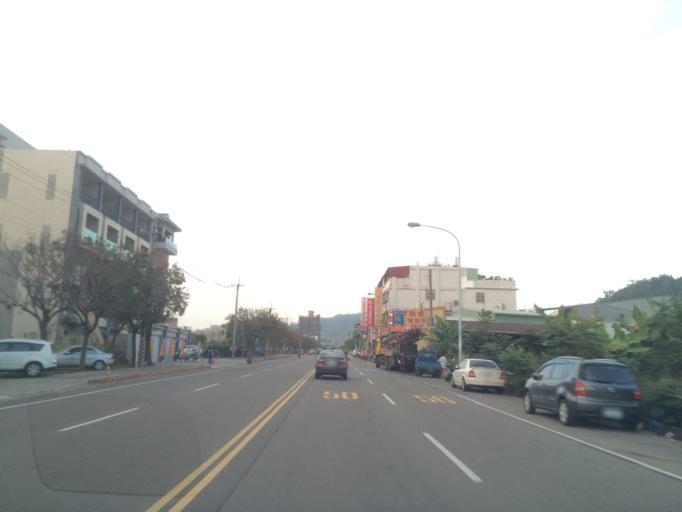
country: TW
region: Taiwan
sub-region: Taichung City
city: Taichung
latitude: 24.1630
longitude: 120.7334
